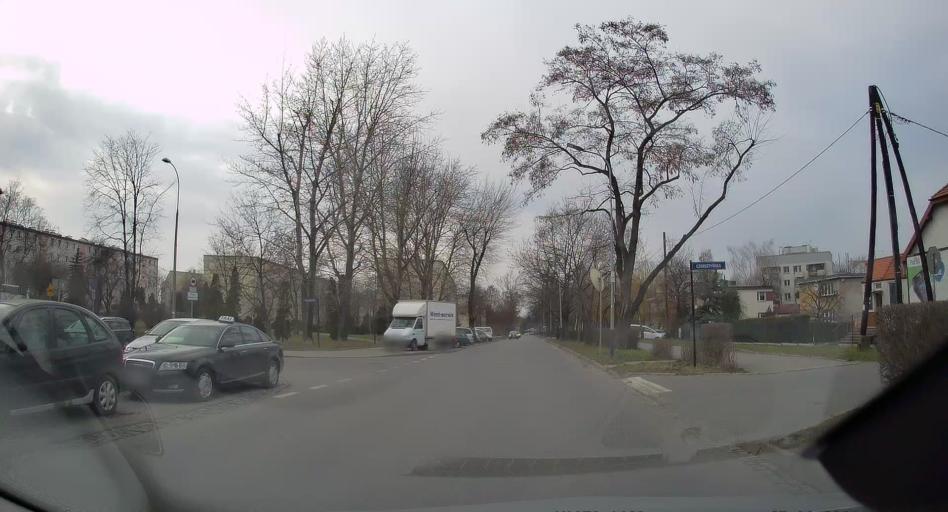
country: PL
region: Lesser Poland Voivodeship
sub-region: Krakow
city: Krakow
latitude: 50.0191
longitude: 19.9816
